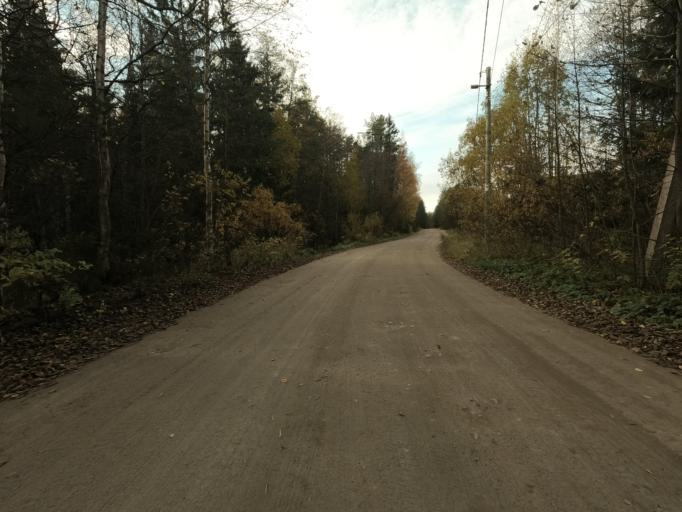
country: RU
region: Leningrad
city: Priladozhskiy
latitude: 59.6301
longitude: 31.3965
